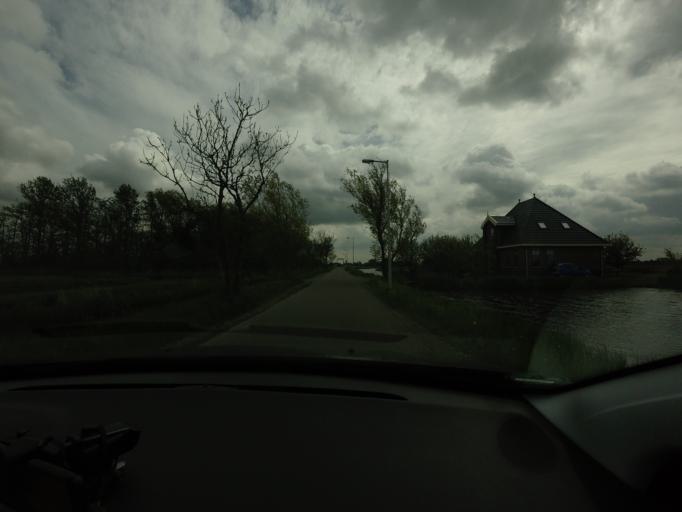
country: NL
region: North Holland
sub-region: Gemeente Landsmeer
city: Landsmeer
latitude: 52.4724
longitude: 4.9012
